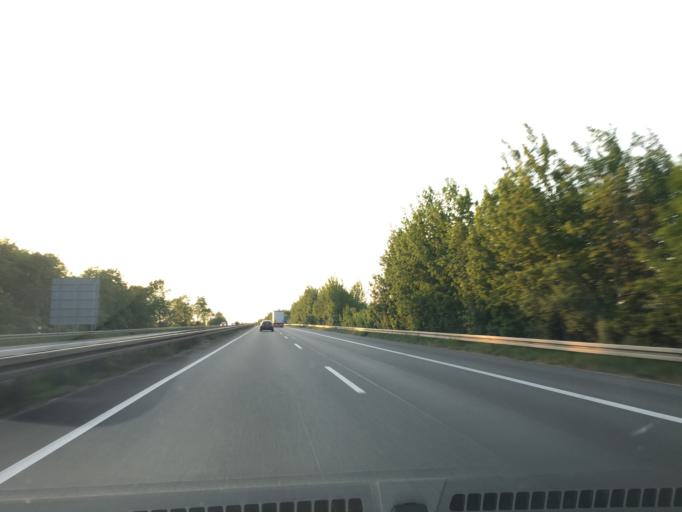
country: DE
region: Lower Saxony
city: Melle
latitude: 52.2003
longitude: 8.3104
